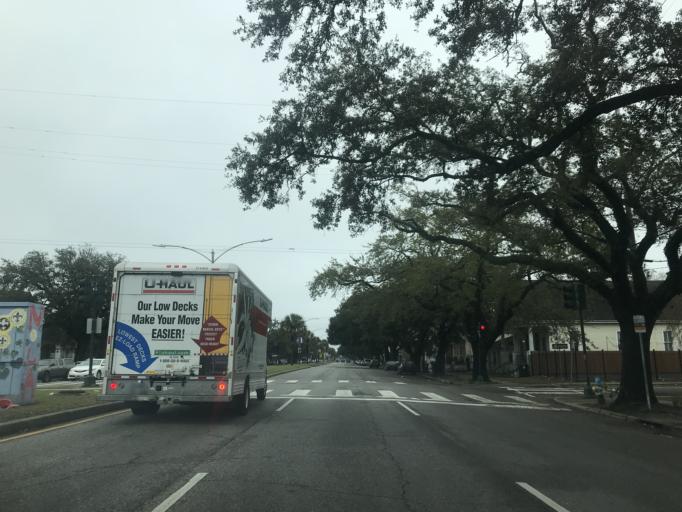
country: US
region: Louisiana
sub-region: Orleans Parish
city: New Orleans
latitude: 29.9695
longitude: -90.1059
